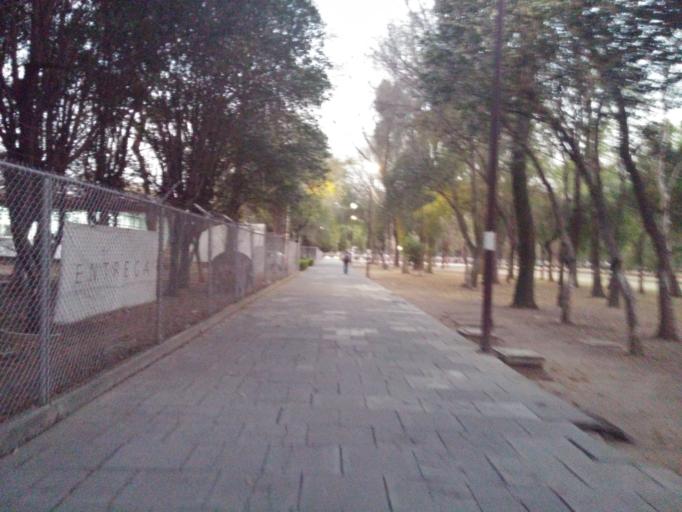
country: MX
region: Mexico
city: Colonia Lindavista
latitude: 19.4981
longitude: -99.1384
